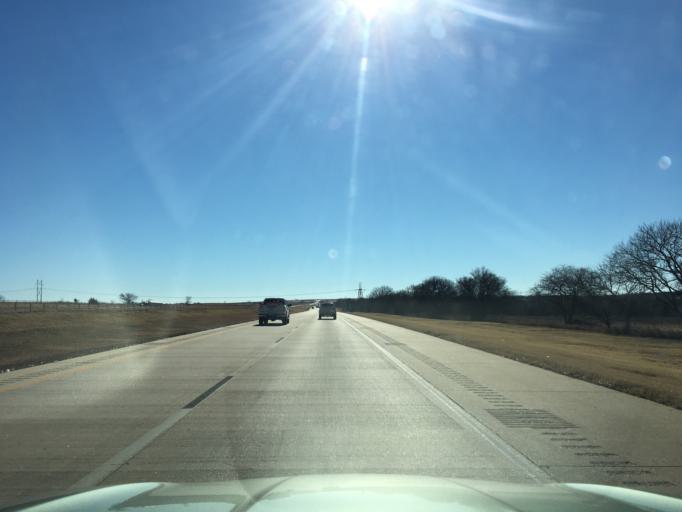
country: US
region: Oklahoma
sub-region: Noble County
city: Perry
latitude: 36.4284
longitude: -97.3272
